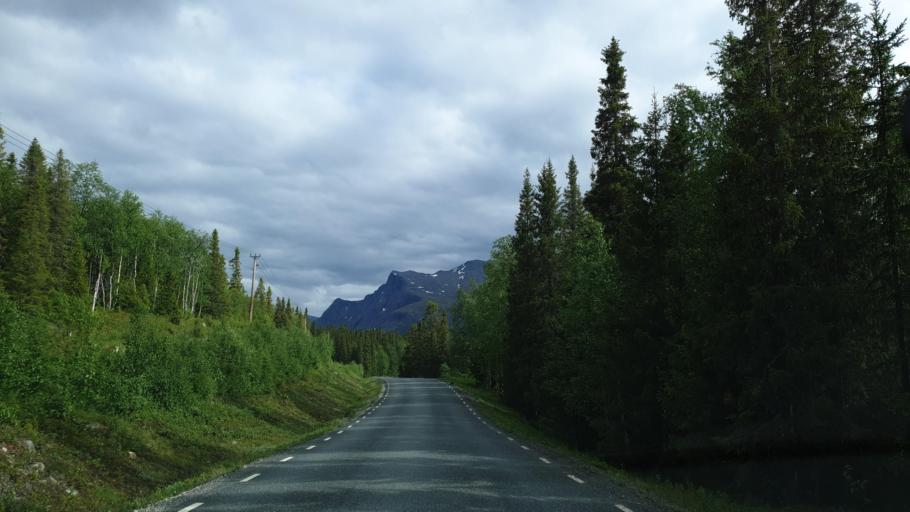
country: SE
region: Vaesterbotten
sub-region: Vilhelmina Kommun
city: Sjoberg
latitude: 65.2653
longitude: 15.3753
